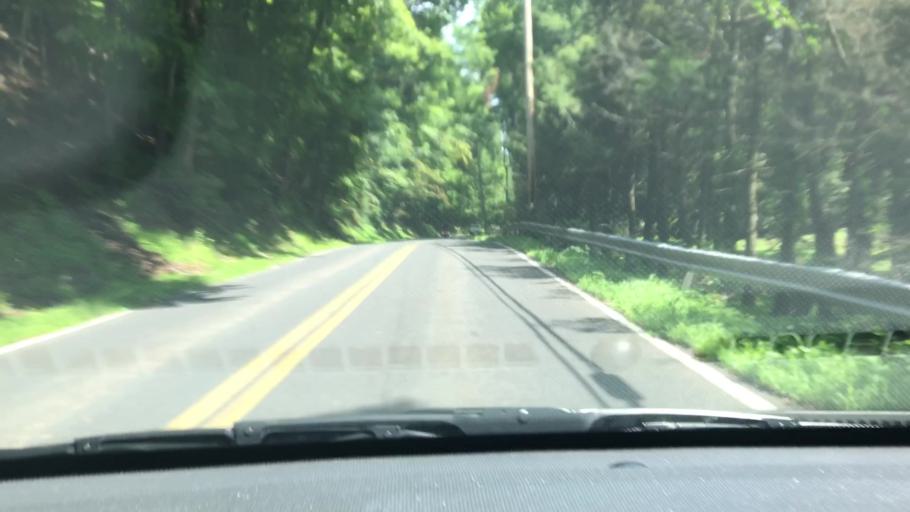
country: US
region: New York
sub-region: Ulster County
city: Stone Ridge
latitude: 41.8898
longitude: -74.1217
